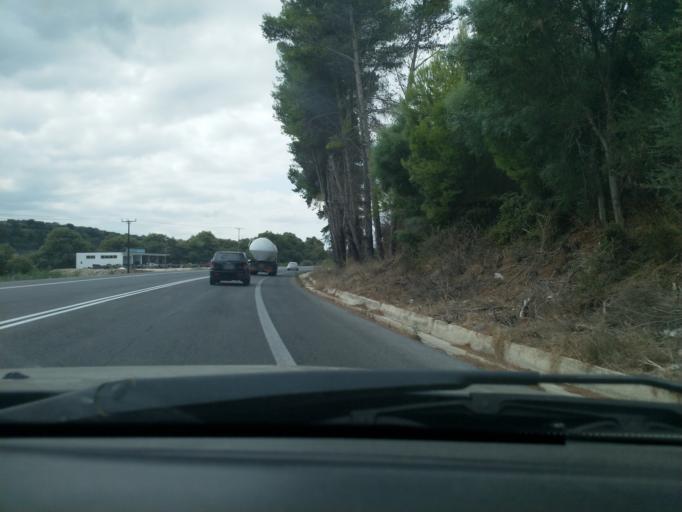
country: GR
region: Crete
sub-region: Nomos Chanias
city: Georgioupolis
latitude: 35.3725
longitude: 24.2123
